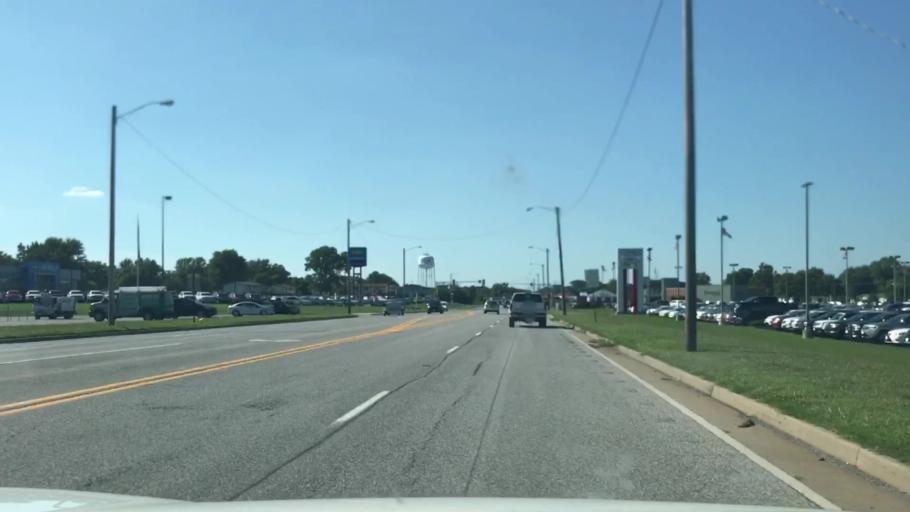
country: US
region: Illinois
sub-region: Madison County
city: Roxana
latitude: 38.8573
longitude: -90.0660
